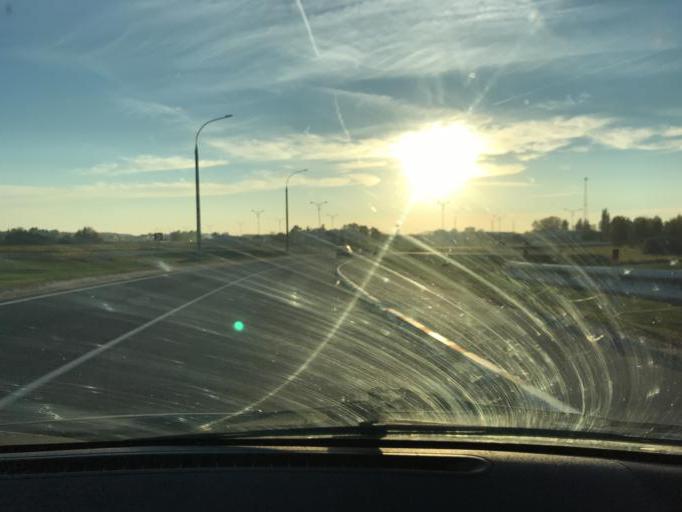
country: BY
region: Brest
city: Horad Kobryn
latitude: 52.2112
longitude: 24.3969
